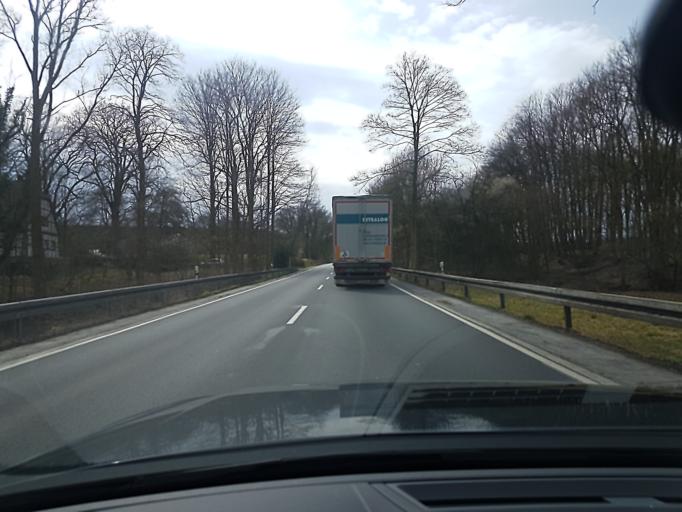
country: DE
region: North Rhine-Westphalia
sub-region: Regierungsbezirk Arnsberg
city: Frondenberg
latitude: 51.4666
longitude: 7.7075
